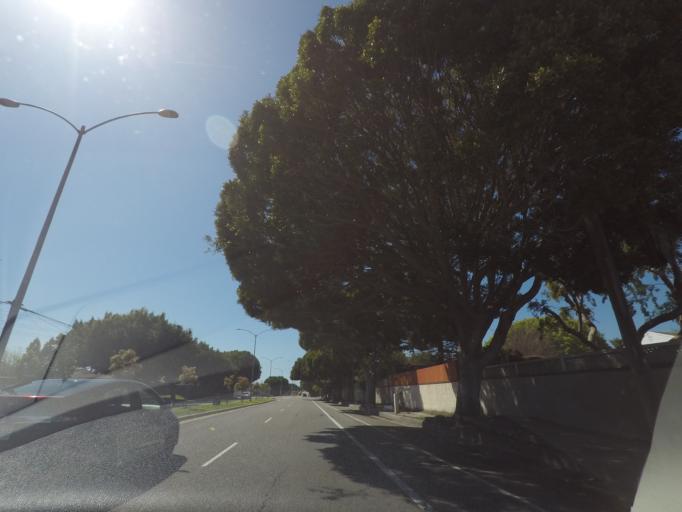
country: US
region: California
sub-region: Los Angeles County
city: Ladera Heights
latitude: 33.9599
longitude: -118.3986
